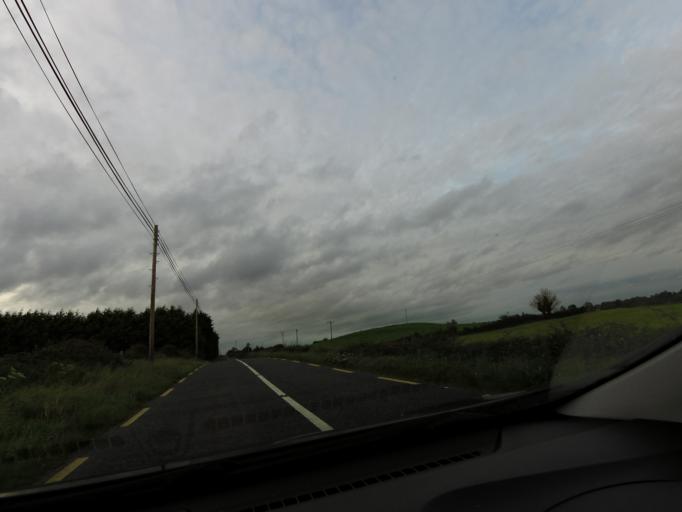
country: IE
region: Leinster
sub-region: An Iarmhi
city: Athlone
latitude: 53.3775
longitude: -7.8612
